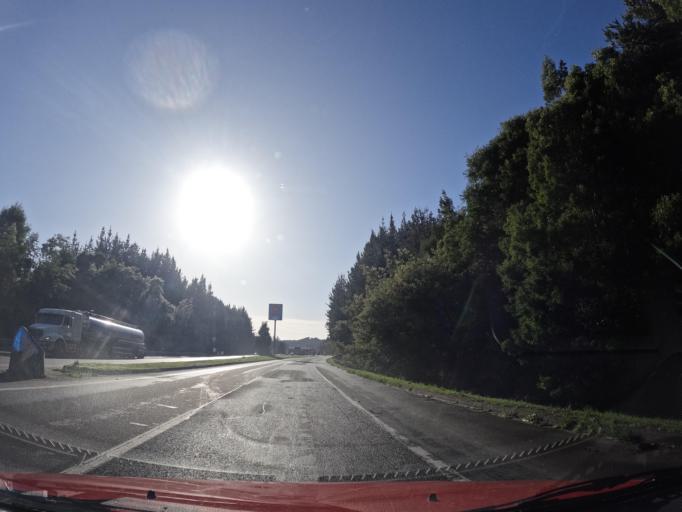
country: CL
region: Biobio
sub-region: Provincia de Concepcion
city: Penco
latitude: -36.7500
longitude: -72.9223
